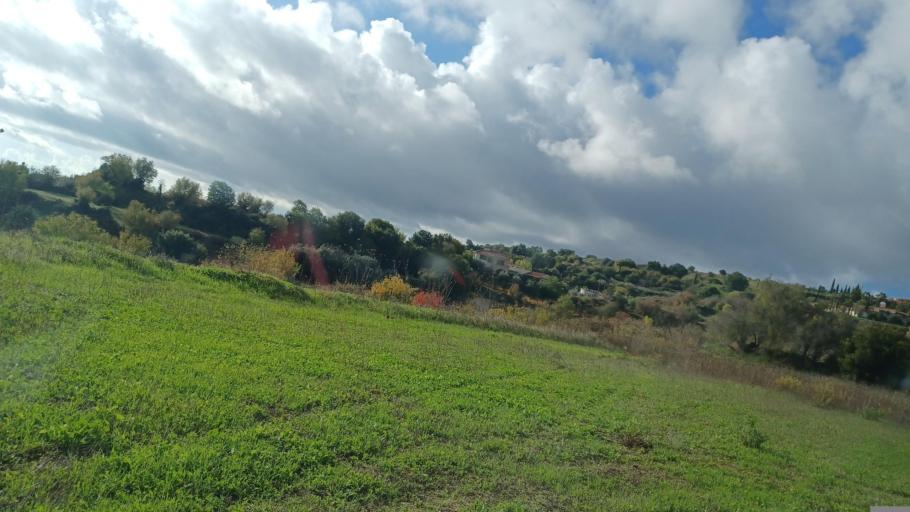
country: CY
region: Pafos
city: Mesogi
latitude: 34.8605
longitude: 32.5061
